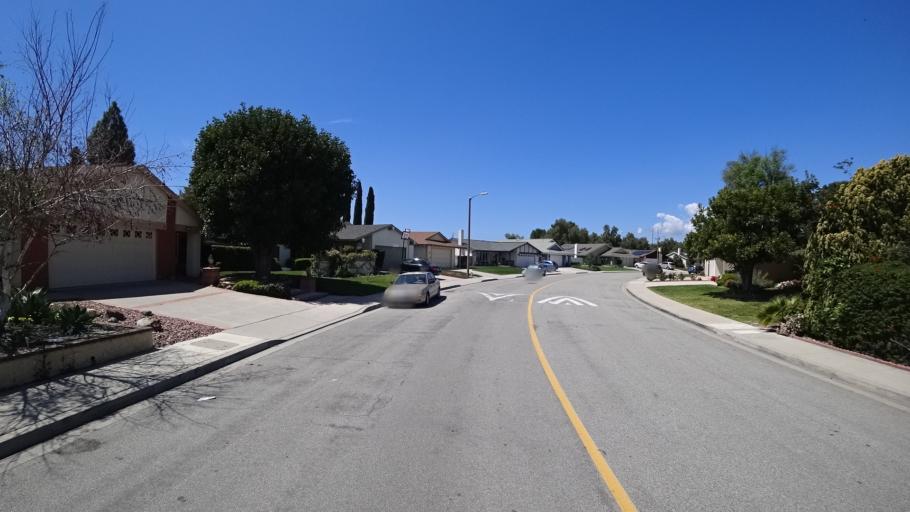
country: US
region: California
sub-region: Ventura County
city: Thousand Oaks
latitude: 34.2132
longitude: -118.8475
